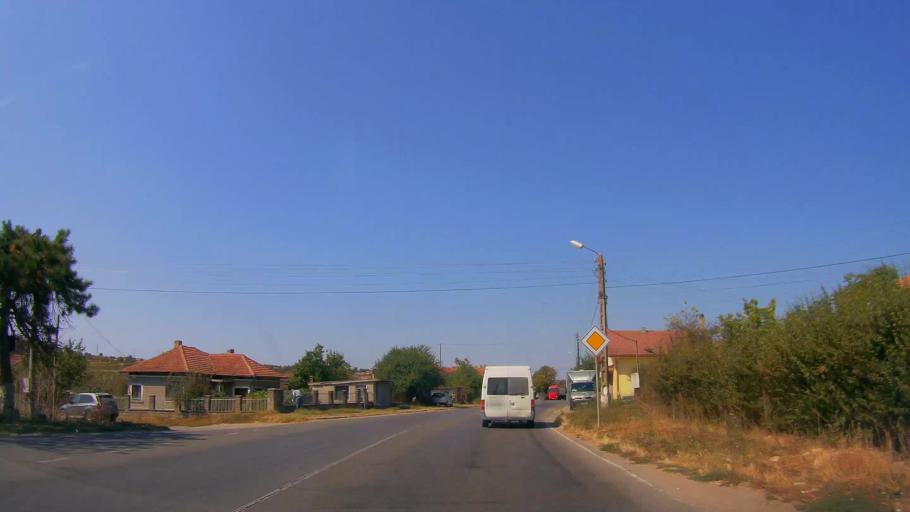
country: BG
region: Razgrad
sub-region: Obshtina Tsar Kaloyan
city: Tsar Kaloyan
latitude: 43.6004
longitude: 26.2458
